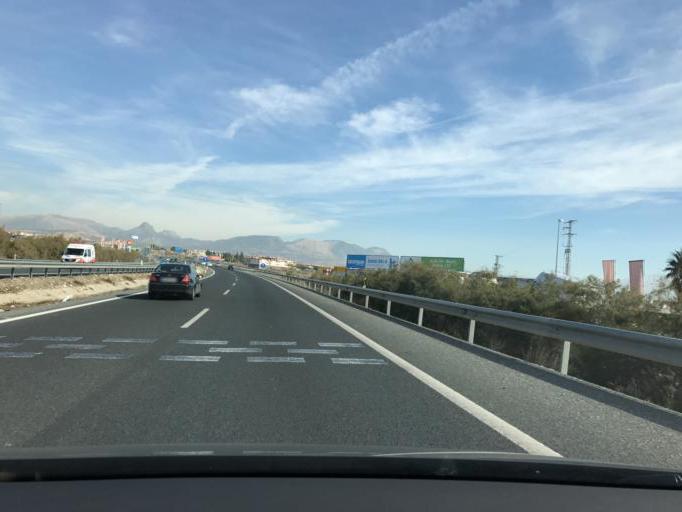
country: ES
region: Andalusia
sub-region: Provincia de Granada
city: Albolote
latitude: 37.2318
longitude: -3.6690
